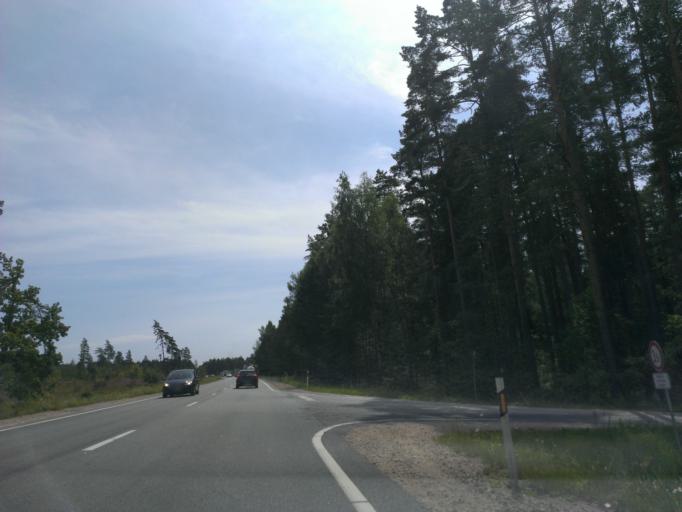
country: LV
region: Salaspils
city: Salaspils
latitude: 56.9249
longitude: 24.3917
